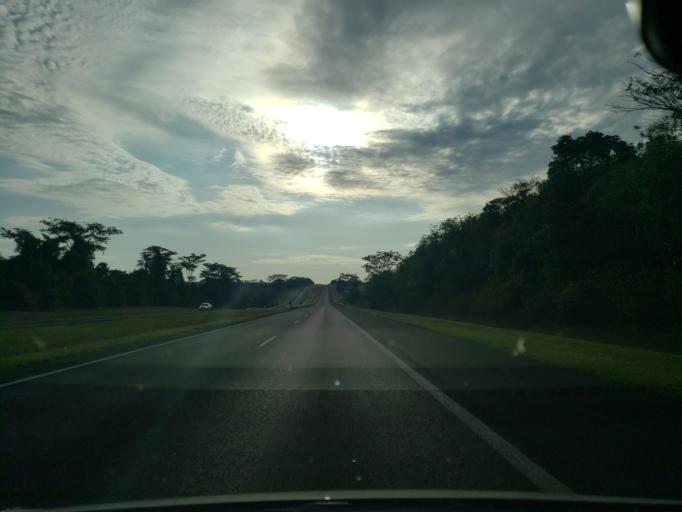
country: BR
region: Sao Paulo
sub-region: Mirandopolis
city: Mirandopolis
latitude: -21.1006
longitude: -51.0398
